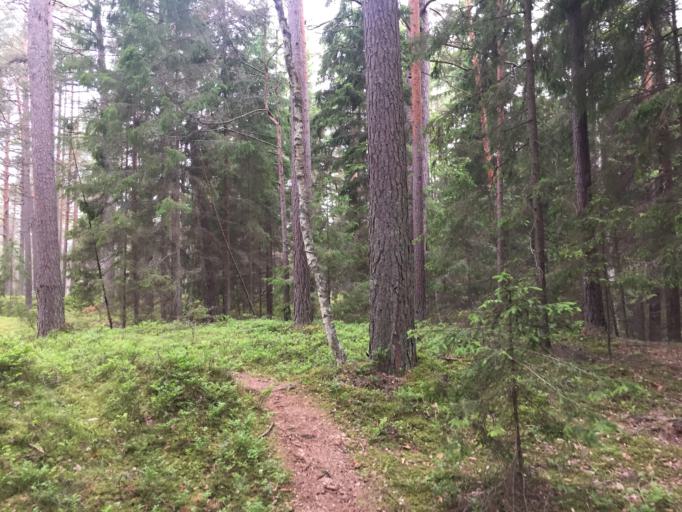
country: LV
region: Tukuma Rajons
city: Engure
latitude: 57.1279
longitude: 23.2335
